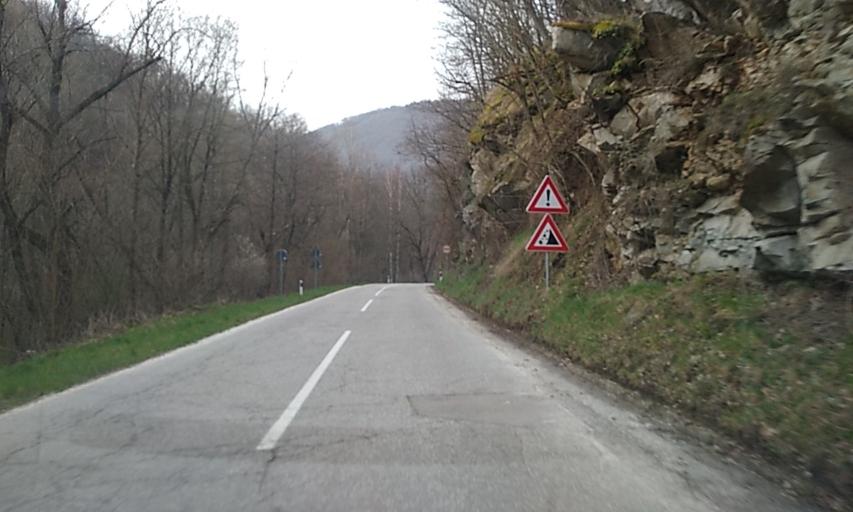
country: RS
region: Central Serbia
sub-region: Pcinjski Okrug
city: Bosilegrad
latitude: 42.5037
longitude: 22.4573
